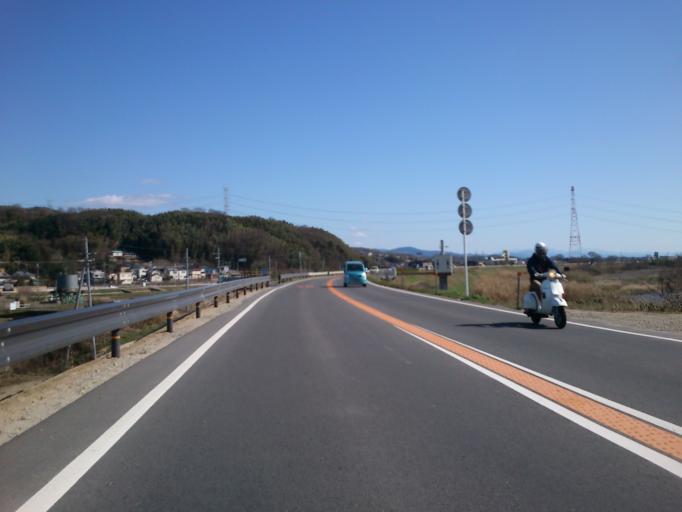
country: JP
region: Kyoto
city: Tanabe
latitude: 34.8128
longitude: 135.8037
